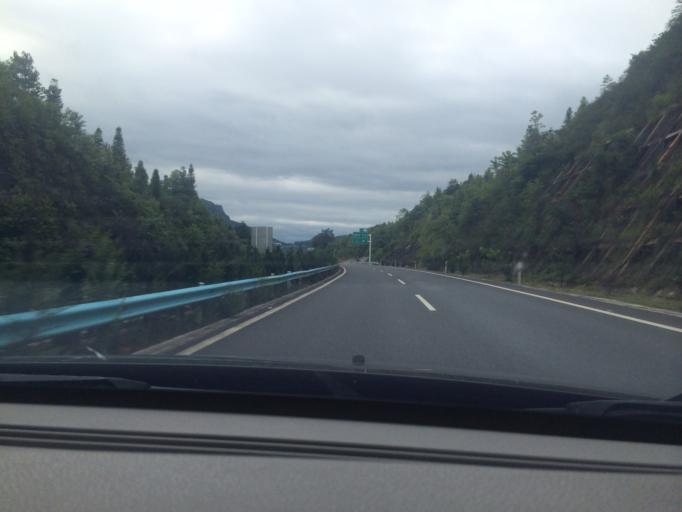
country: CN
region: Guangxi Zhuangzu Zizhiqu
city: Xinzhou
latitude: 25.5454
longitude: 105.1439
